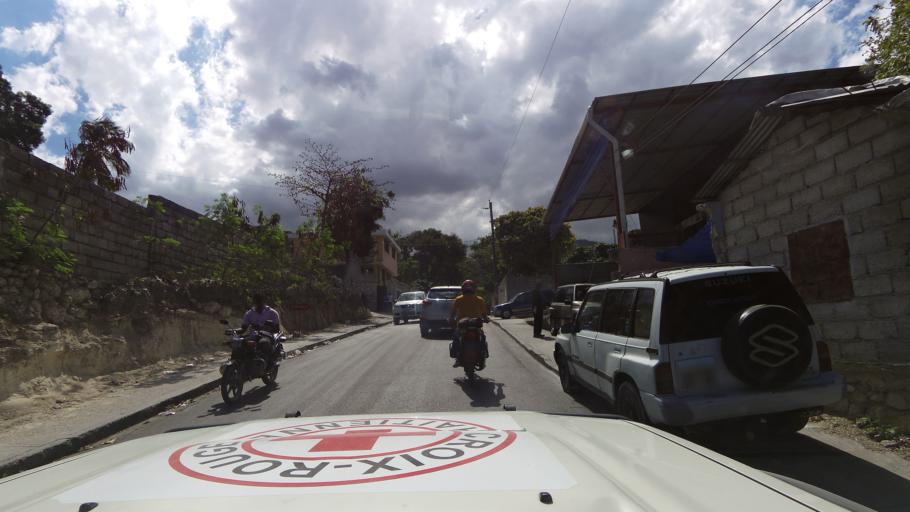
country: HT
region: Ouest
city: Delmas 73
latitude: 18.5340
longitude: -72.2964
